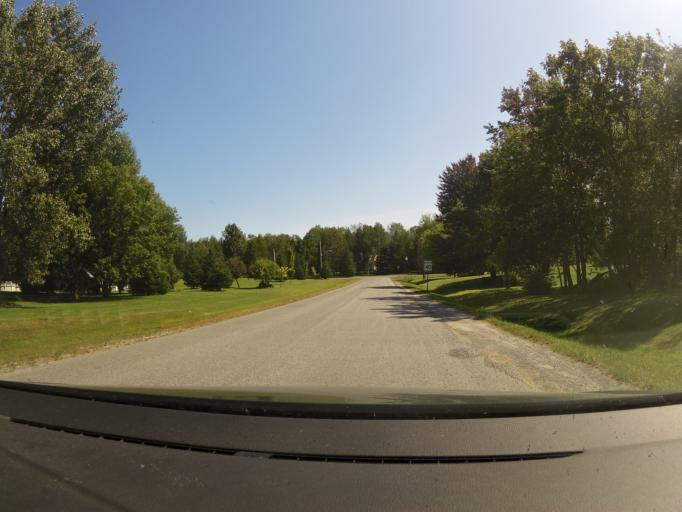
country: CA
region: Ontario
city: Bells Corners
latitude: 45.2867
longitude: -75.9995
